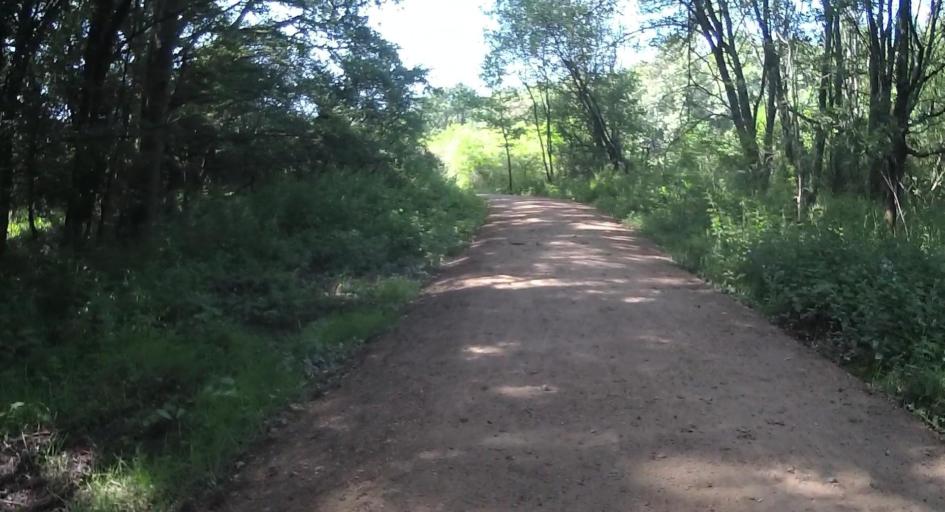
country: GB
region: England
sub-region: Hampshire
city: Kingsley
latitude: 51.1485
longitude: -0.8673
